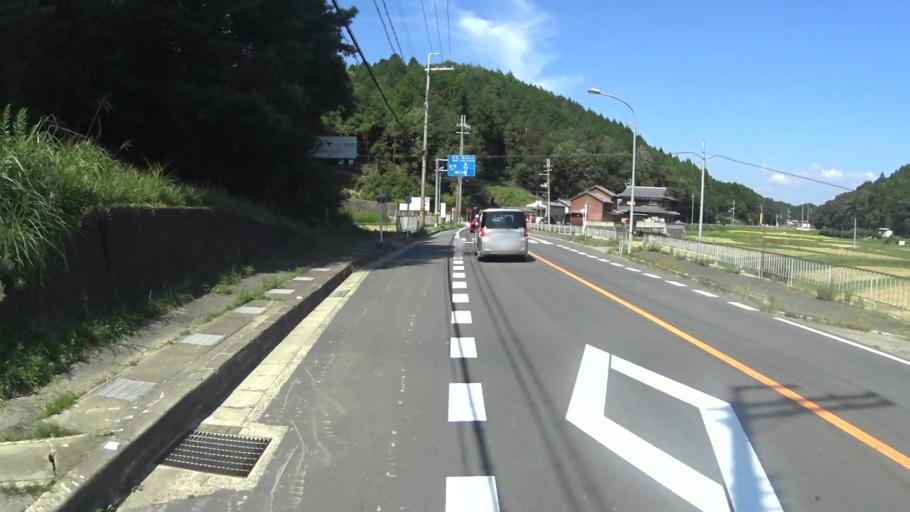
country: JP
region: Kyoto
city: Kameoka
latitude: 34.9716
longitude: 135.5173
